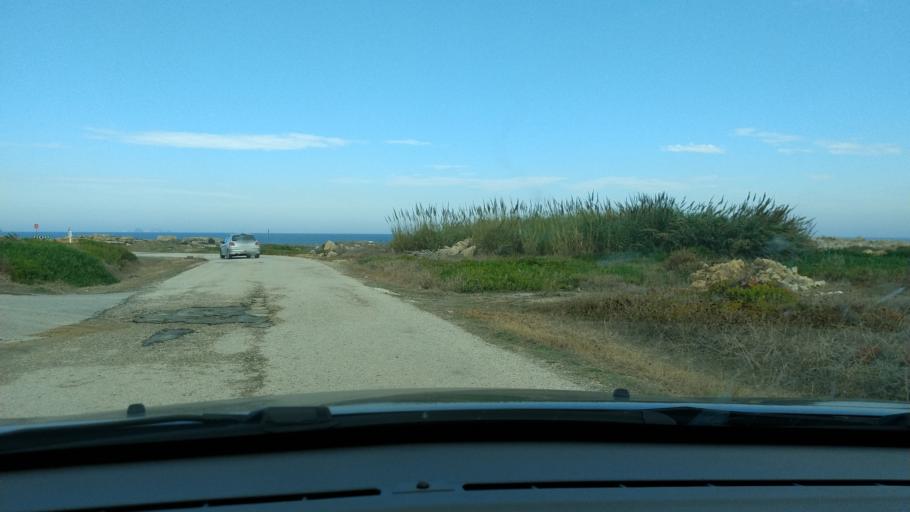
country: PT
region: Leiria
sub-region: Peniche
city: Peniche
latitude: 39.3665
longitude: -9.4010
